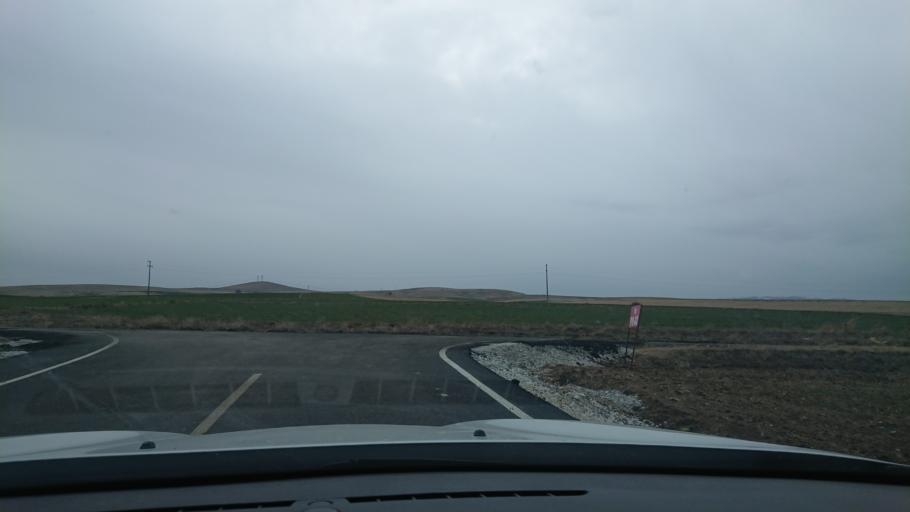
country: TR
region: Aksaray
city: Agacoren
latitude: 38.9439
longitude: 33.9109
